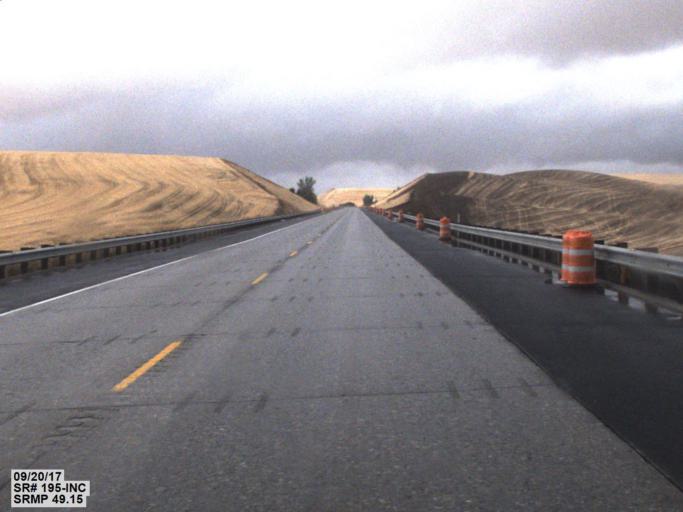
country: US
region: Washington
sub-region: Whitman County
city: Colfax
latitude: 47.0224
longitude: -117.3586
